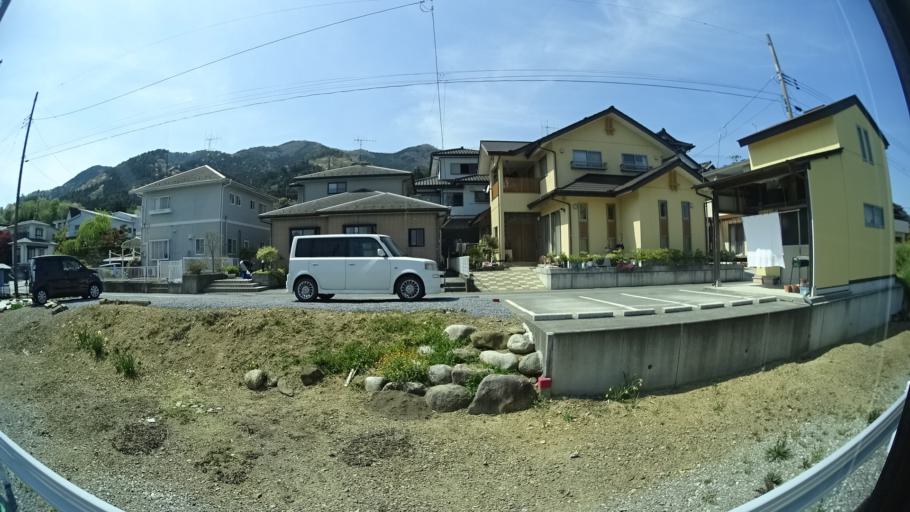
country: JP
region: Iwate
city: Ofunato
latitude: 39.0386
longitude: 141.7212
